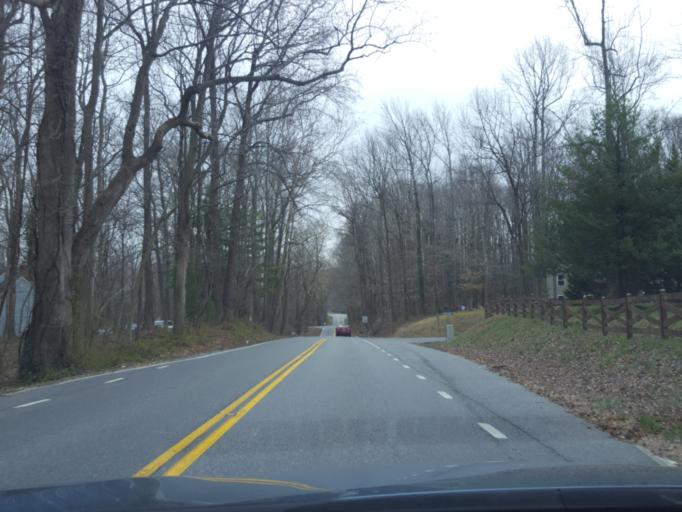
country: US
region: Maryland
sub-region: Calvert County
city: North Beach
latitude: 38.7118
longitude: -76.5519
